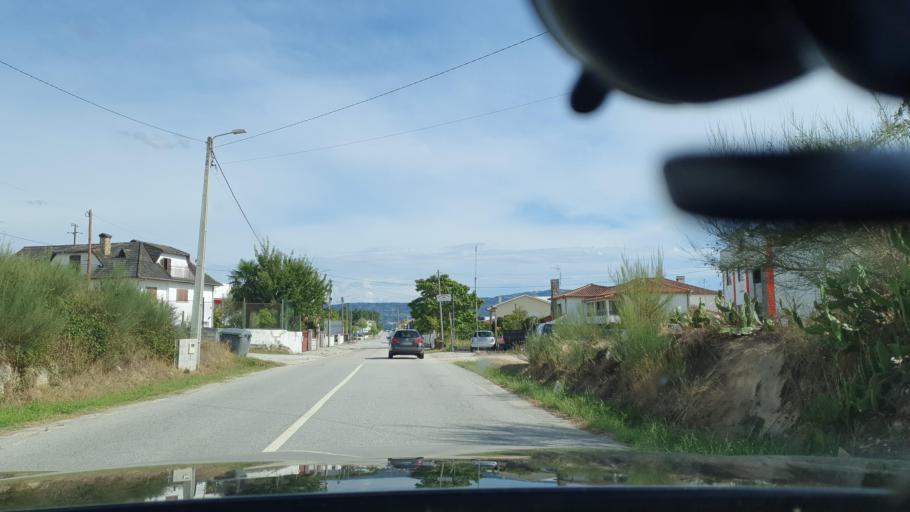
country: PT
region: Vila Real
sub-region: Chaves
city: Chaves
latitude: 41.7704
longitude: -7.4865
